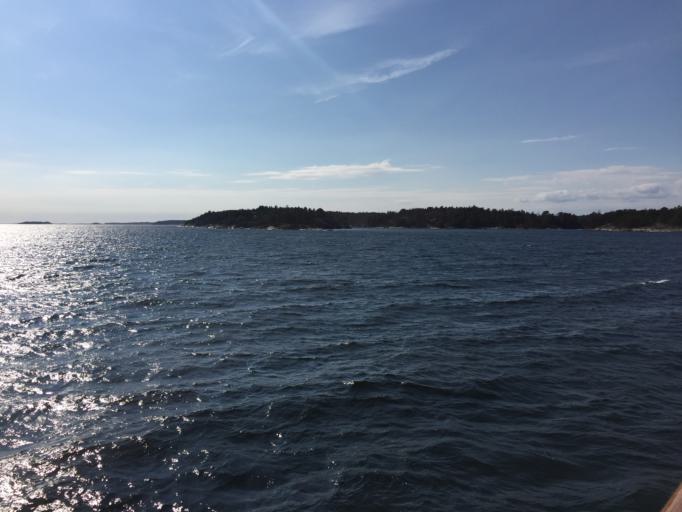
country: SE
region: Stockholm
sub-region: Varmdo Kommun
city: Holo
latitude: 59.2820
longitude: 18.7201
